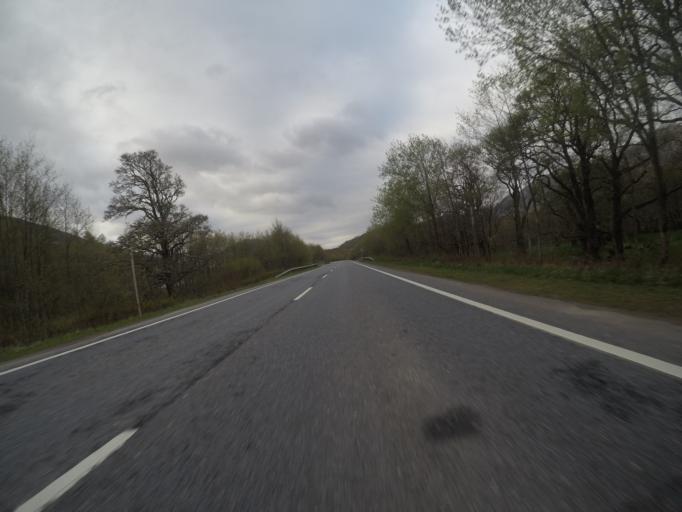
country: GB
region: Scotland
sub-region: Highland
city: Spean Bridge
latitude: 56.9498
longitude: -4.4978
